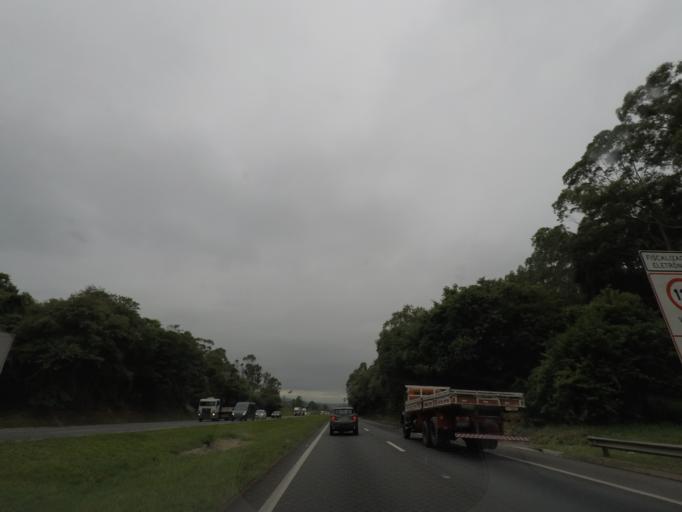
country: BR
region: Sao Paulo
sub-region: Jarinu
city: Jarinu
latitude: -23.0357
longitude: -46.7236
